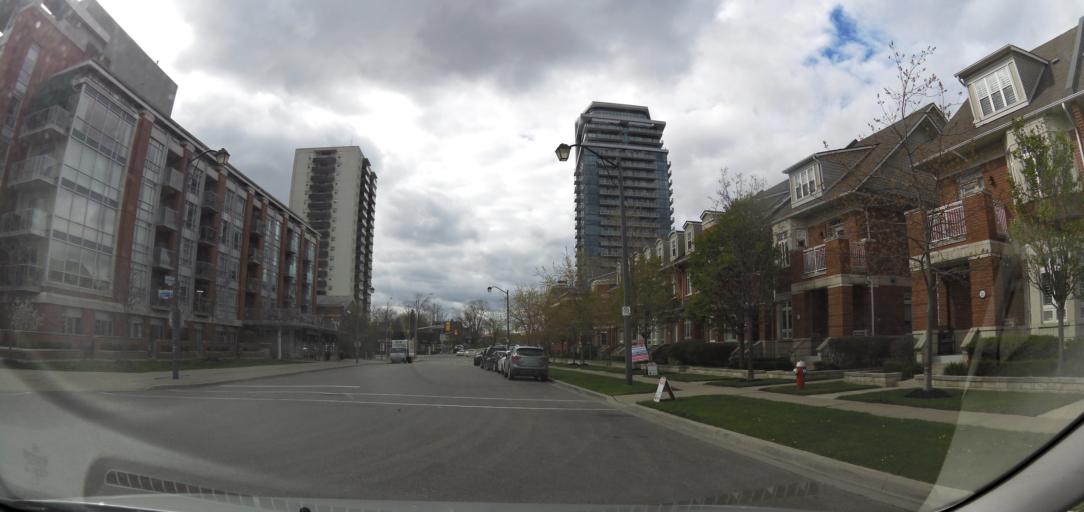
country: CA
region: Ontario
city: Mississauga
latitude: 43.5546
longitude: -79.5807
